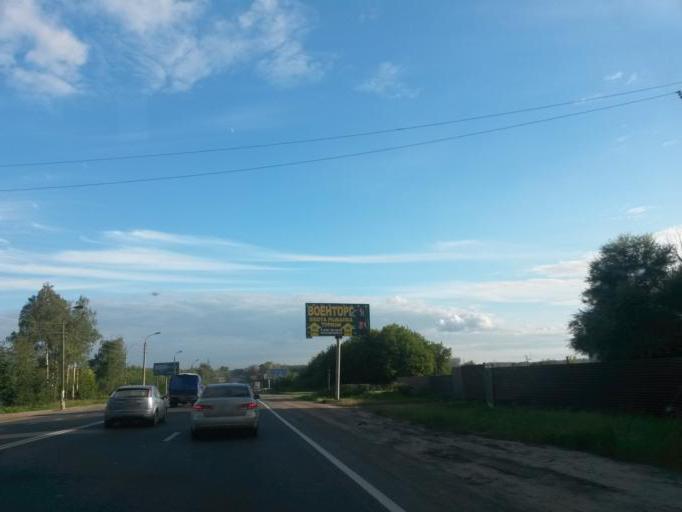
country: RU
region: Moskovskaya
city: Petrovskaya
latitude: 55.5450
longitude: 37.7735
